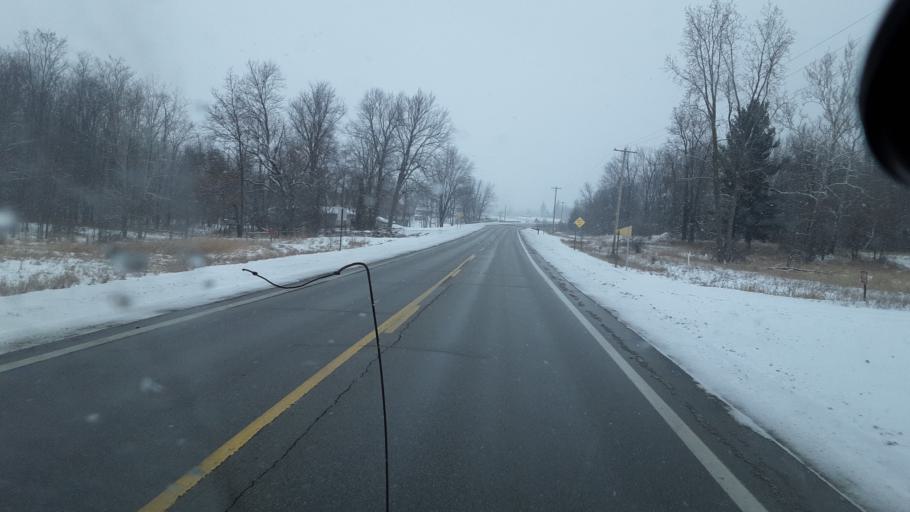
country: US
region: Michigan
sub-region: Jackson County
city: Jackson
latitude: 42.3098
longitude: -84.3881
